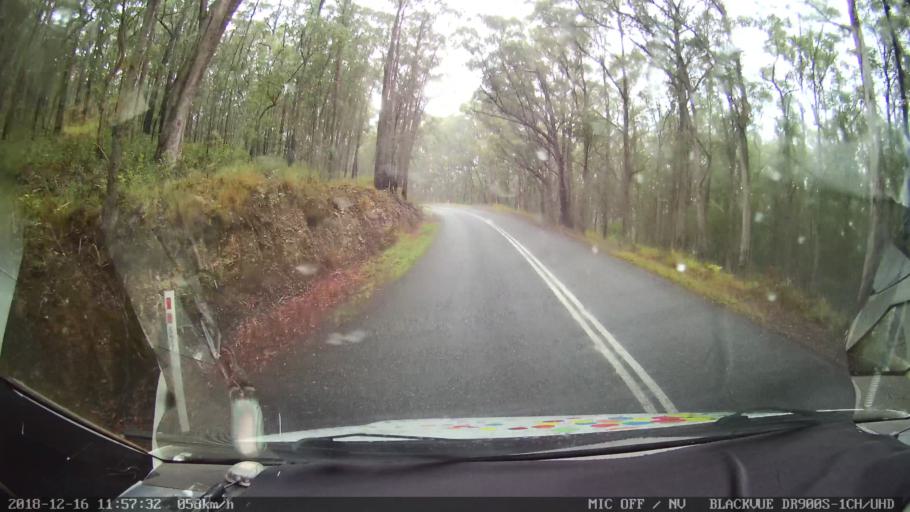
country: AU
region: New South Wales
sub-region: Tenterfield Municipality
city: Carrolls Creek
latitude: -28.9171
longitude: 152.3082
